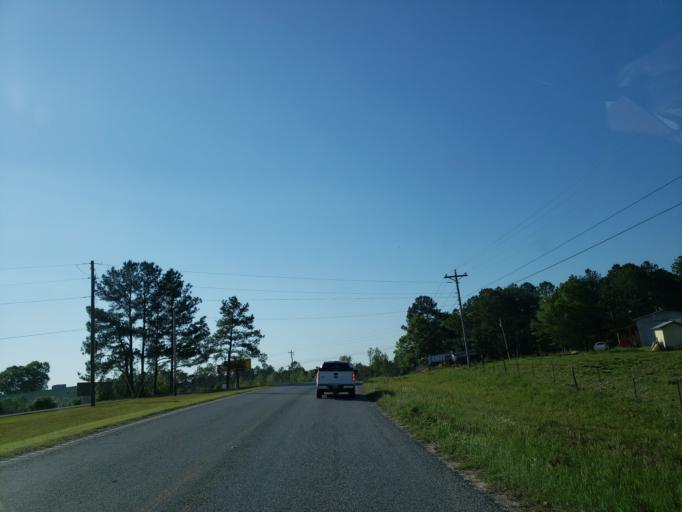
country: US
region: Mississippi
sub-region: Perry County
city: Richton
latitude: 31.4815
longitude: -89.0154
